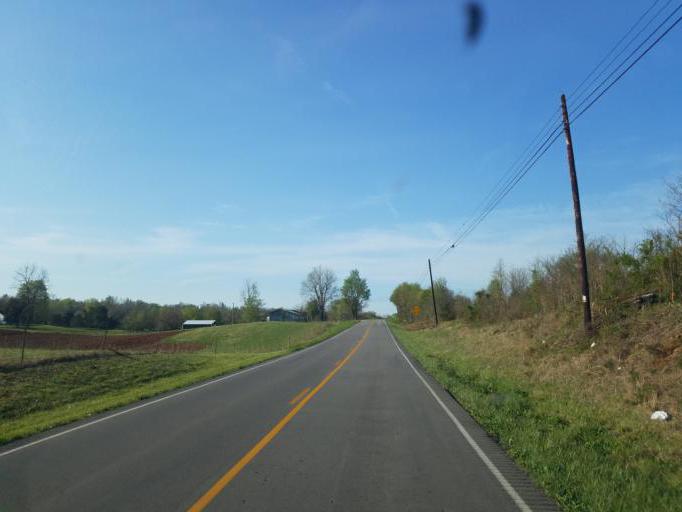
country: US
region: Kentucky
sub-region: Hart County
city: Munfordville
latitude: 37.4029
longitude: -85.8978
